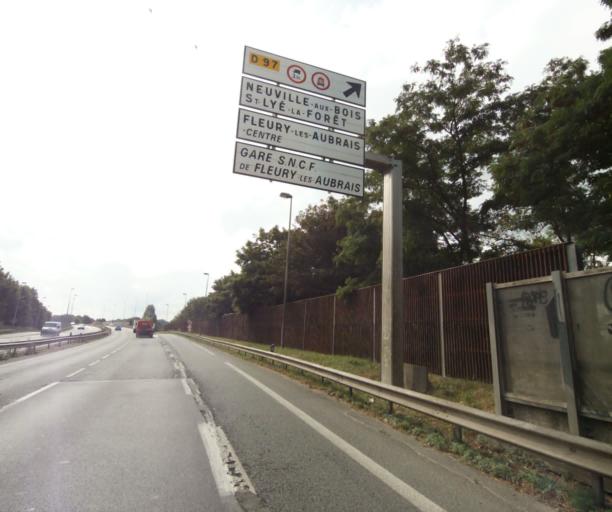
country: FR
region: Centre
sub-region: Departement du Loiret
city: Fleury-les-Aubrais
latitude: 47.9385
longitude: 1.9149
